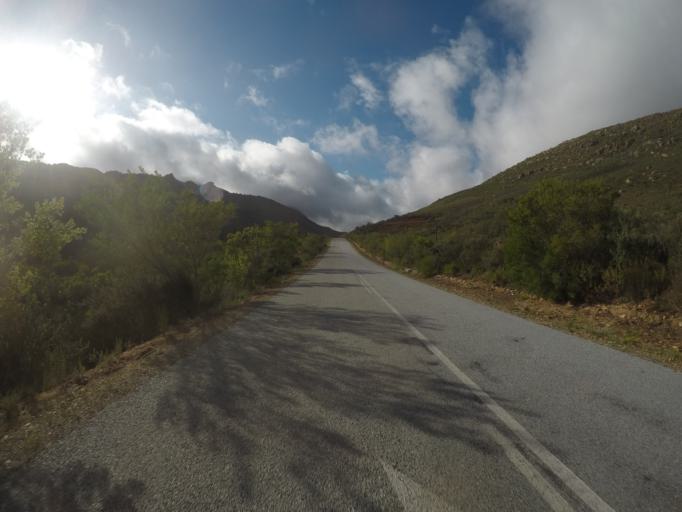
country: ZA
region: Western Cape
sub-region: West Coast District Municipality
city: Clanwilliam
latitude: -32.3655
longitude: 18.8592
